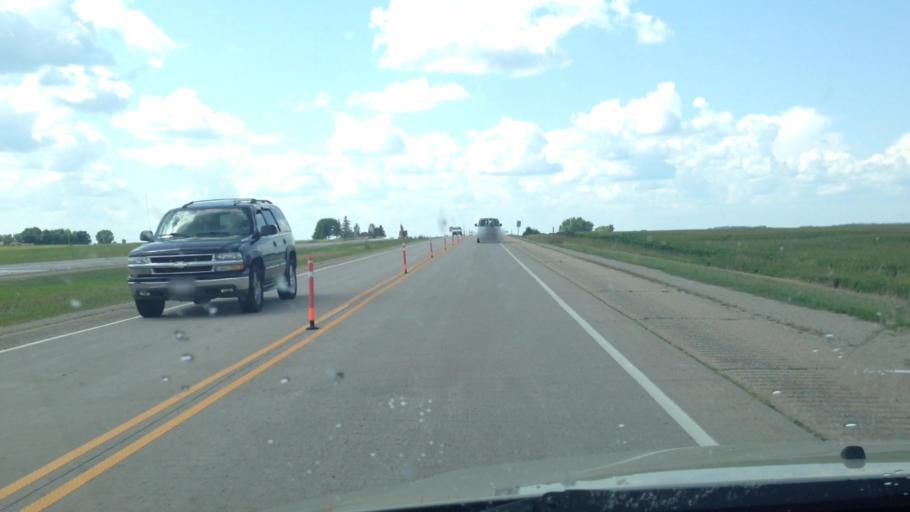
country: US
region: Wisconsin
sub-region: Shawano County
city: Bonduel
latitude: 44.6990
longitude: -88.3568
